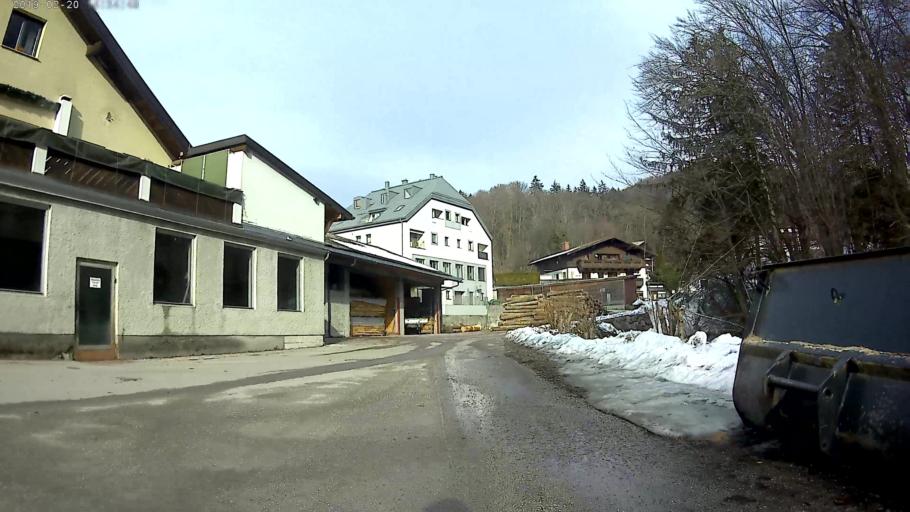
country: AT
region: Salzburg
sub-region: Politischer Bezirk Salzburg-Umgebung
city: Elsbethen
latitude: 47.7692
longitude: 13.0875
